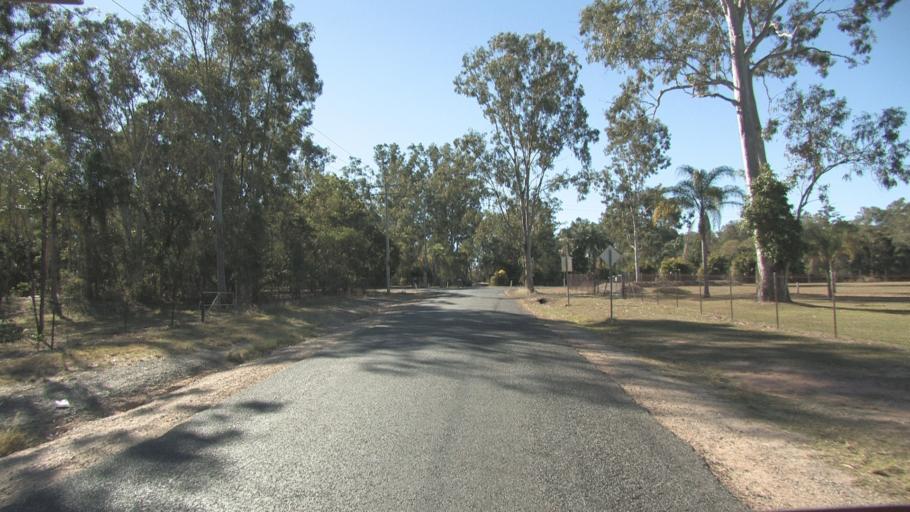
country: AU
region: Queensland
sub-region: Logan
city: Park Ridge South
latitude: -27.7218
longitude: 152.9914
